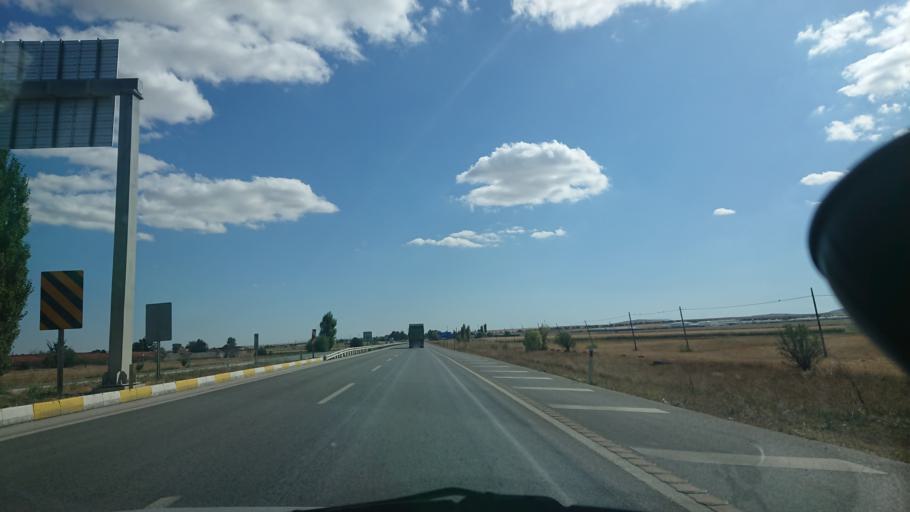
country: TR
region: Eskisehir
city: Mahmudiye
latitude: 39.5687
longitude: 30.9139
